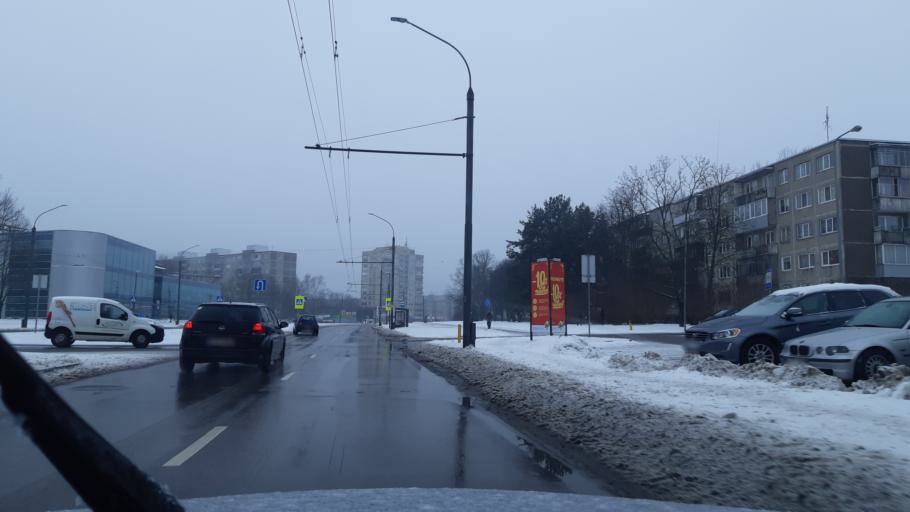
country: LT
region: Kauno apskritis
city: Dainava (Kaunas)
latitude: 54.9171
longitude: 23.9665
